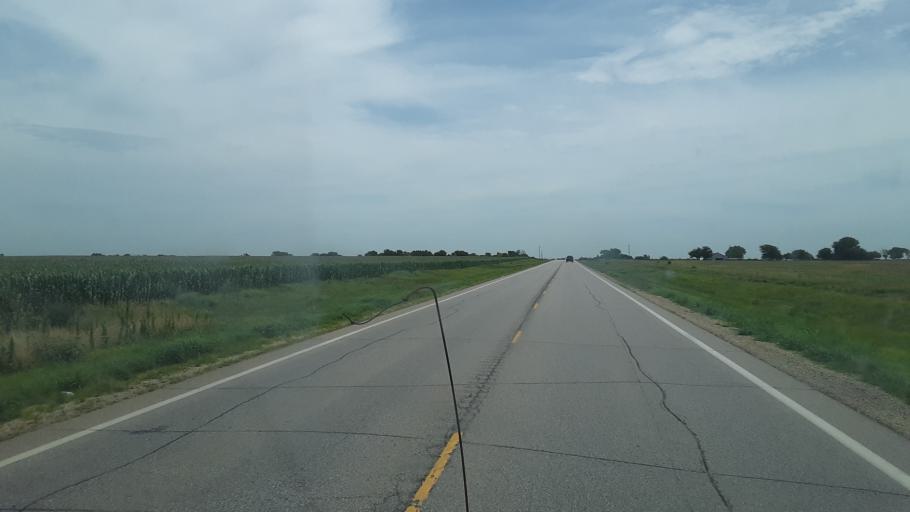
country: US
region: Kansas
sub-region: Butler County
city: El Dorado
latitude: 37.8106
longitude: -96.7144
